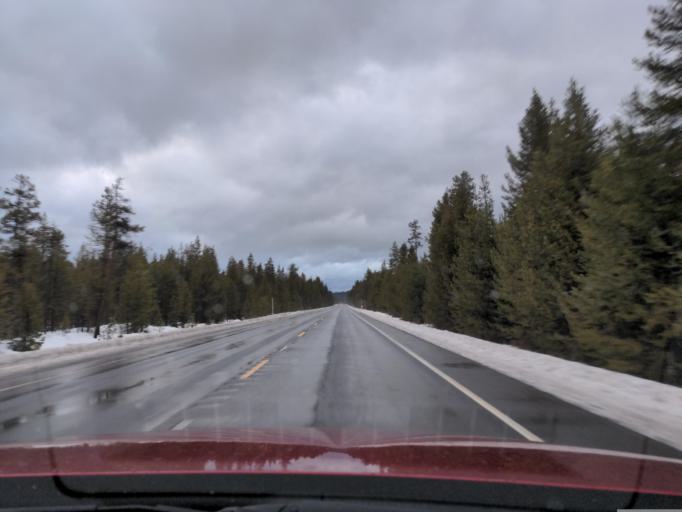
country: US
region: Oregon
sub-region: Deschutes County
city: La Pine
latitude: 43.4074
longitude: -121.8279
